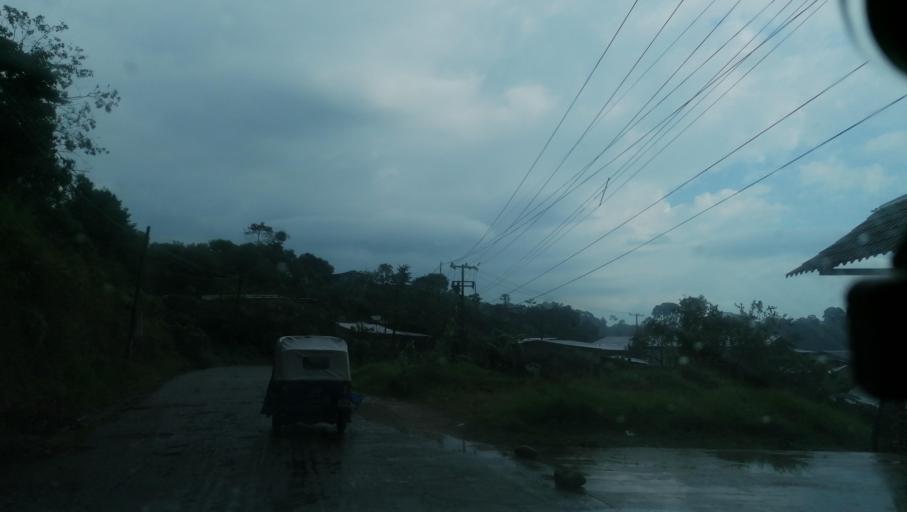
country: MX
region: Chiapas
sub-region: Cacahoatan
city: Benito Juarez
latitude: 15.0533
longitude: -92.1904
